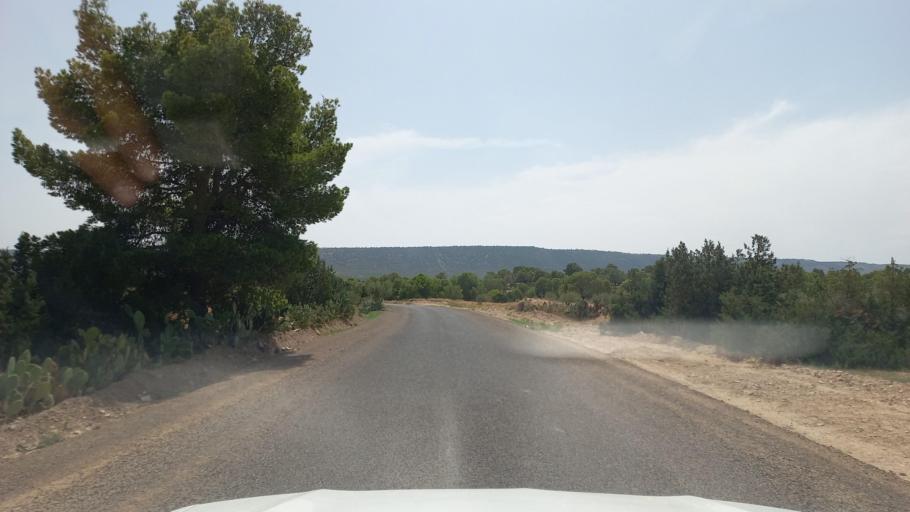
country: TN
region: Al Qasrayn
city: Sbiba
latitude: 35.3955
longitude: 8.9485
